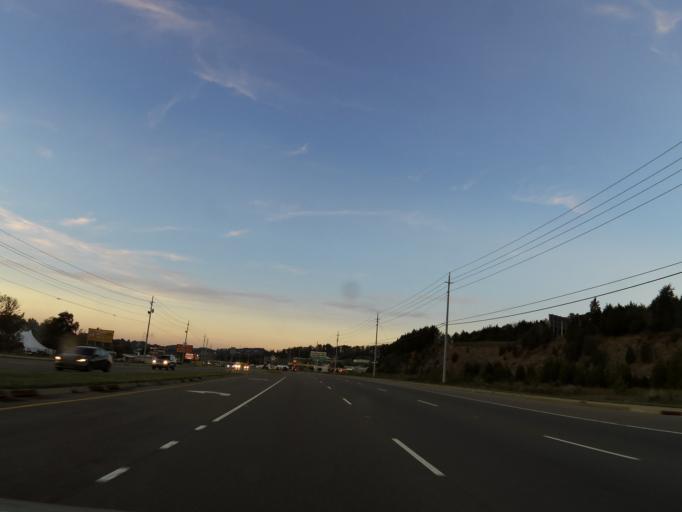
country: US
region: Tennessee
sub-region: Sevier County
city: Sevierville
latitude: 35.9153
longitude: -83.5805
